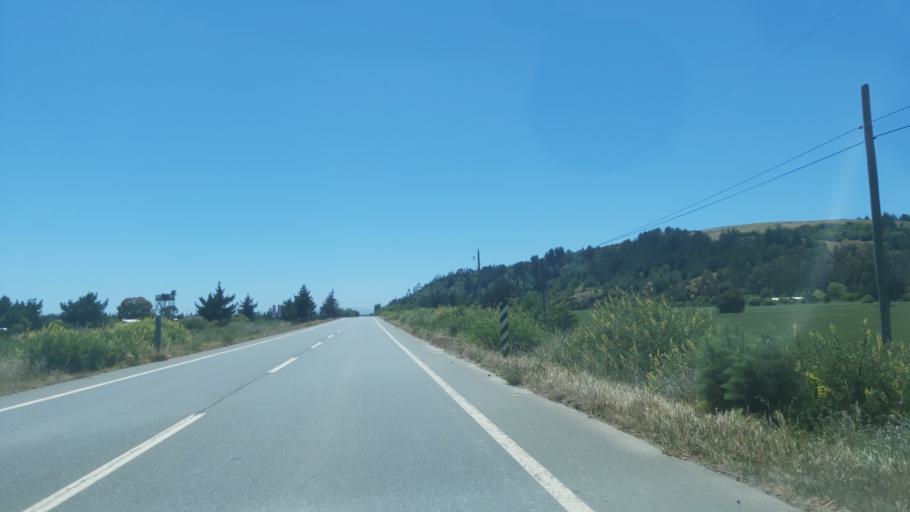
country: CL
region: Maule
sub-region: Provincia de Talca
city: Constitucion
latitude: -35.1693
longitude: -72.2652
